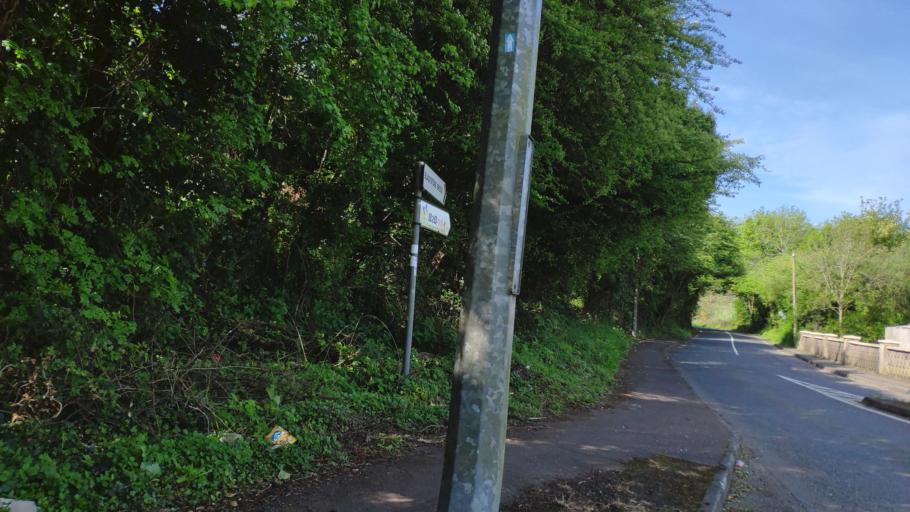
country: IE
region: Munster
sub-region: County Cork
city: Cork
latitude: 51.9235
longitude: -8.4938
